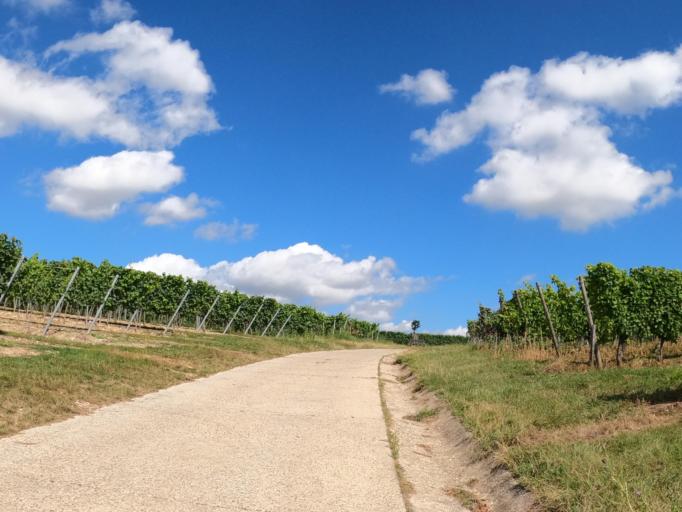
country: DE
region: Rheinland-Pfalz
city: Bissersheim
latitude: 49.5299
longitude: 8.2050
